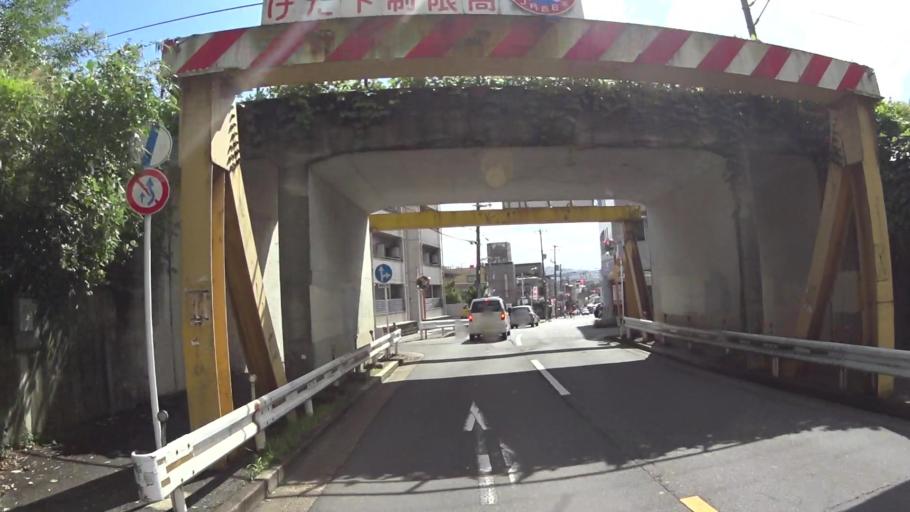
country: JP
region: Kyoto
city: Uji
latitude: 34.9329
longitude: 135.7833
